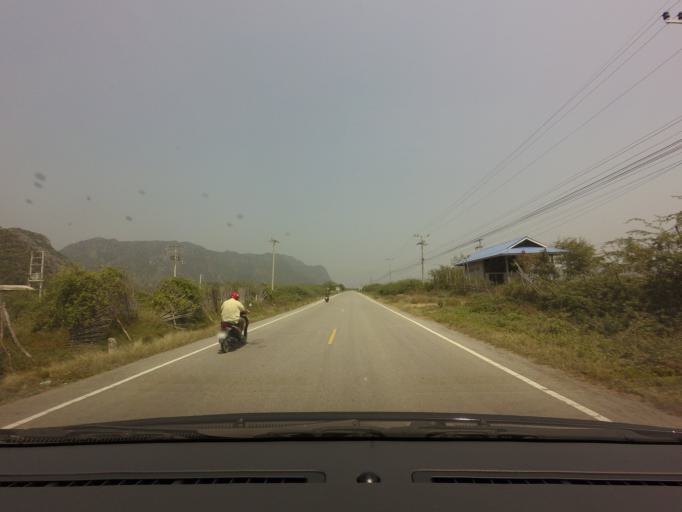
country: TH
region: Prachuap Khiri Khan
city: Kui Buri
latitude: 12.1431
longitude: 99.9647
